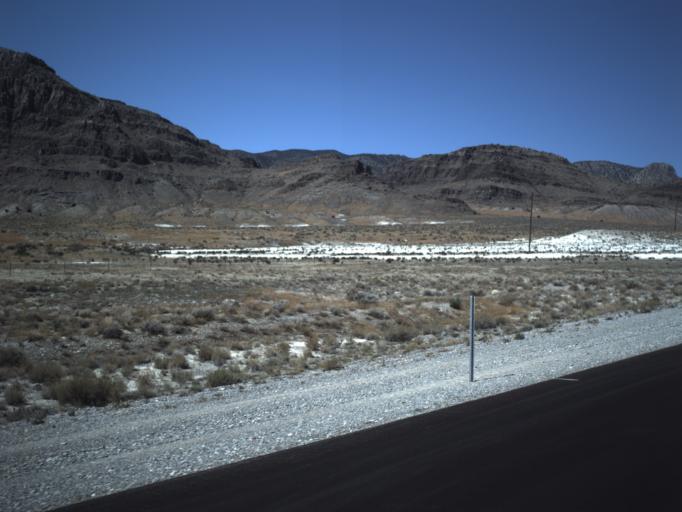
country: US
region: Utah
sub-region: Beaver County
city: Milford
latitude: 39.0835
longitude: -113.4973
